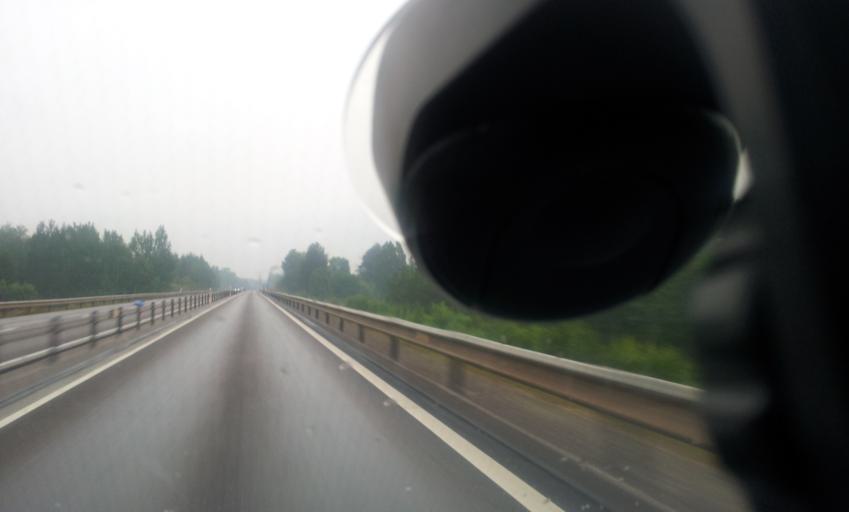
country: SE
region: Kalmar
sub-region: Vasterviks Kommun
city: Vaestervik
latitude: 57.7532
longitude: 16.5573
